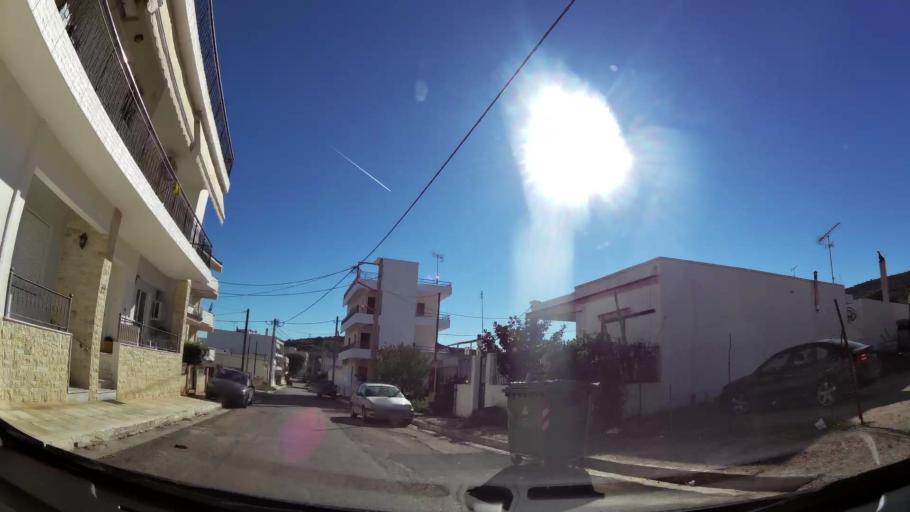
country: GR
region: Attica
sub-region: Nomarchia Anatolikis Attikis
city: Koropi
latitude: 37.8961
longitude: 23.8629
